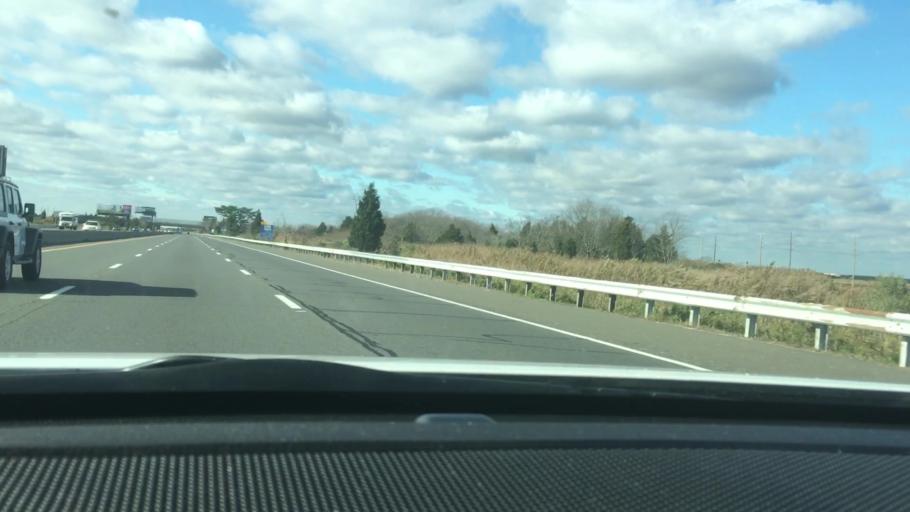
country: US
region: New Jersey
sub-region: Atlantic County
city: Ventnor City
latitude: 39.3726
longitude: -74.4715
